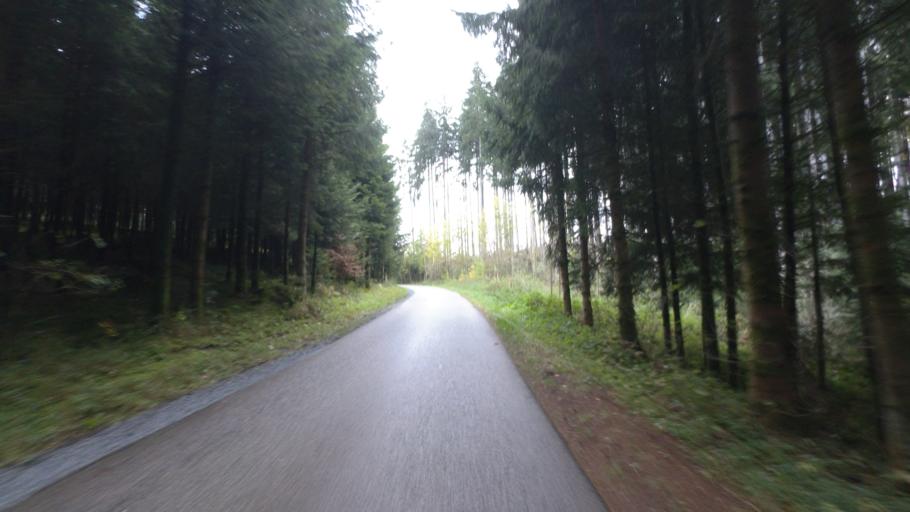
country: DE
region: Bavaria
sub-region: Upper Bavaria
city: Nussdorf
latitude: 47.9135
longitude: 12.5936
